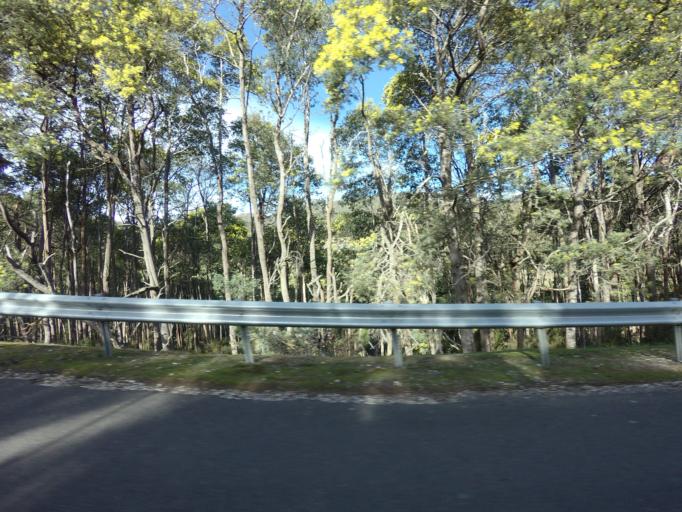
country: AU
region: Tasmania
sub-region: Huon Valley
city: Cygnet
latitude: -43.1740
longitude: 147.1622
